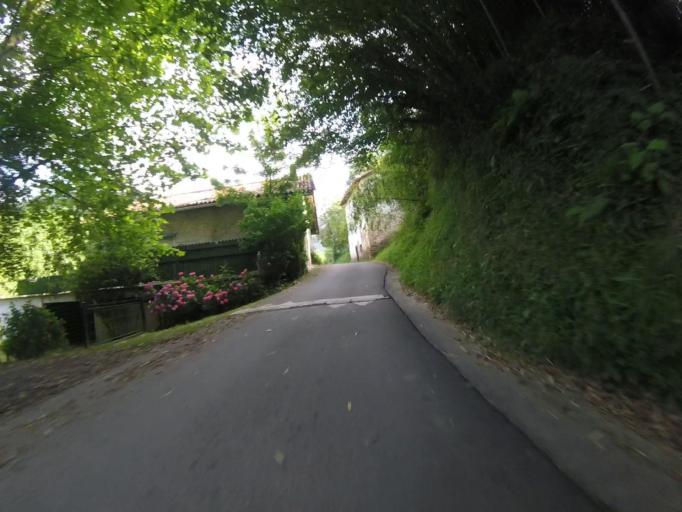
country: ES
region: Basque Country
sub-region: Provincia de Guipuzcoa
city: Astigarraga
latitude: 43.2529
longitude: -1.9502
